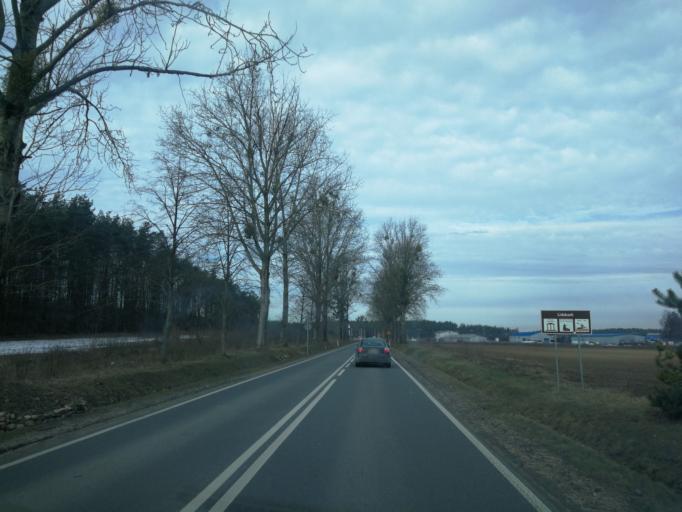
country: PL
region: Warmian-Masurian Voivodeship
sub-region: Powiat dzialdowski
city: Lidzbark
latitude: 53.2585
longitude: 19.8636
